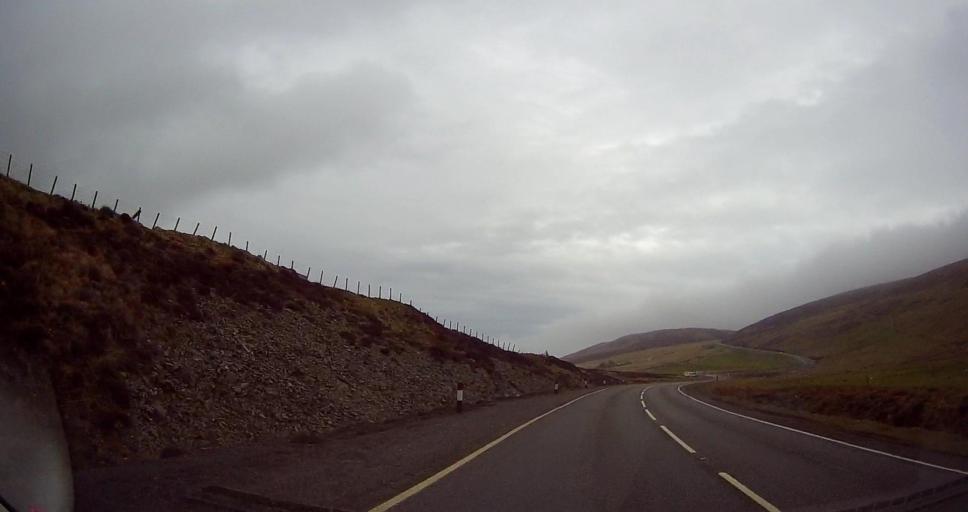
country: GB
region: Scotland
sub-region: Shetland Islands
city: Lerwick
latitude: 60.1583
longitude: -1.2318
